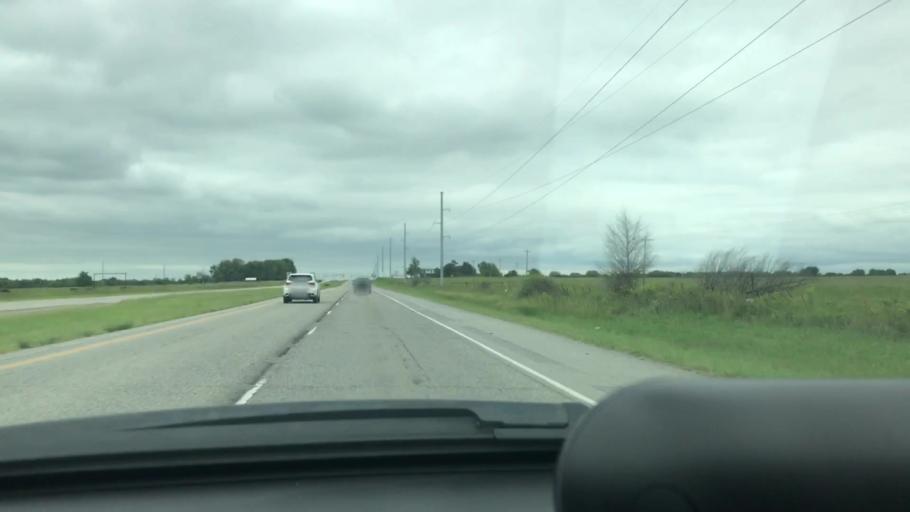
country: US
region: Oklahoma
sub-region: Wagoner County
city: Wagoner
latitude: 36.0101
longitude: -95.3686
